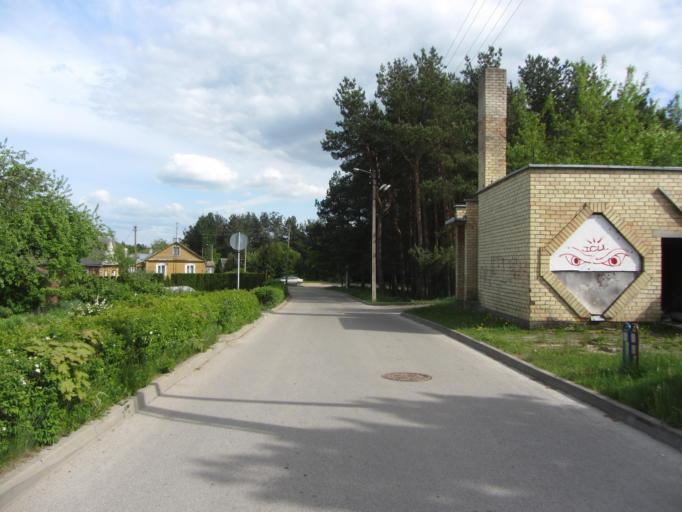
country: LT
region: Utenos apskritis
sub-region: Utena
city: Utena
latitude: 55.4948
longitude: 25.5905
